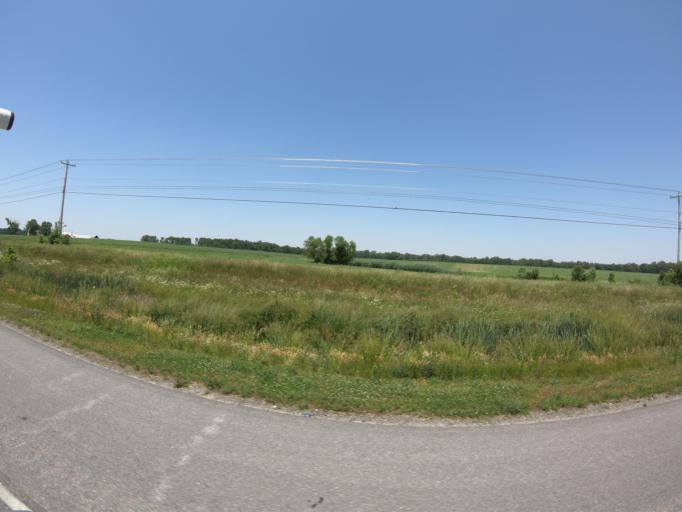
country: US
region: Maryland
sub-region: Caroline County
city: Ridgely
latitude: 38.9269
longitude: -75.9921
